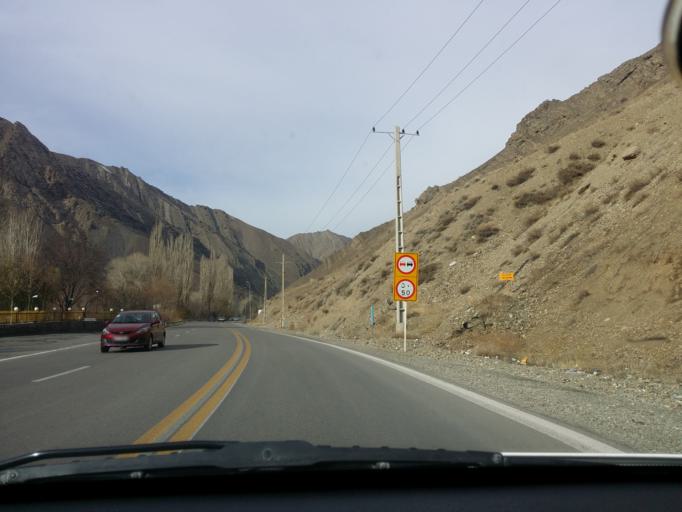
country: IR
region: Alborz
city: Karaj
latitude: 36.0318
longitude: 51.2150
